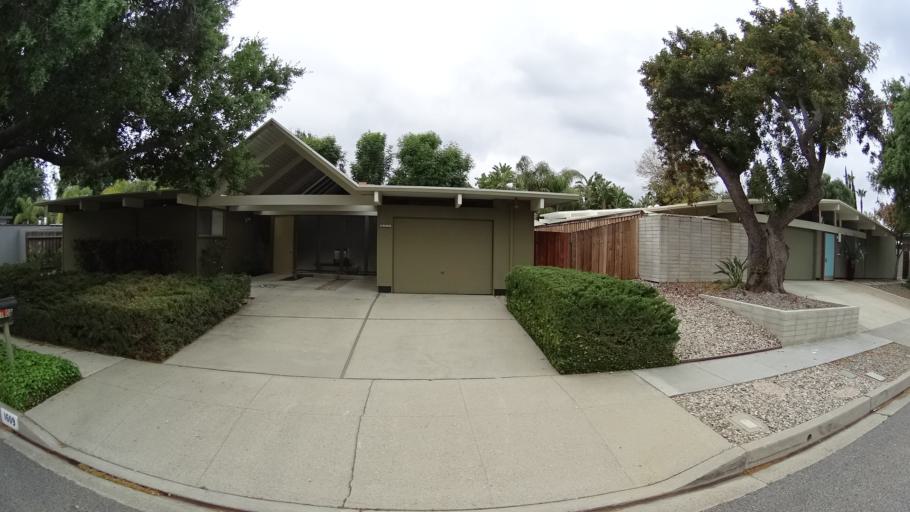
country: US
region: California
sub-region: Ventura County
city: Casa Conejo
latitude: 34.2006
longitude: -118.8886
